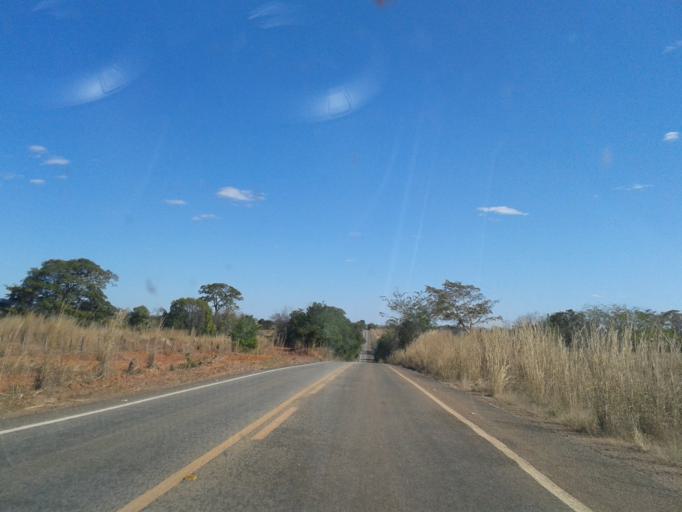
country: BR
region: Goias
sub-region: Mozarlandia
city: Mozarlandia
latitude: -14.4707
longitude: -50.4707
